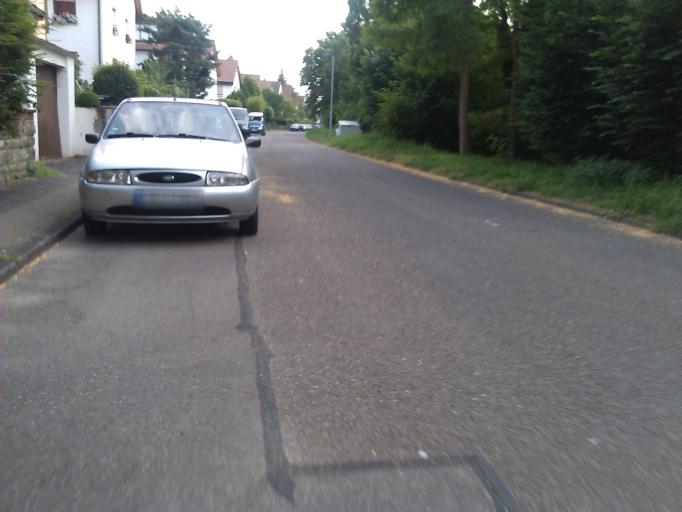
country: DE
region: Baden-Wuerttemberg
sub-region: Regierungsbezirk Stuttgart
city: Heilbronn
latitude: 49.1315
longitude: 9.2072
